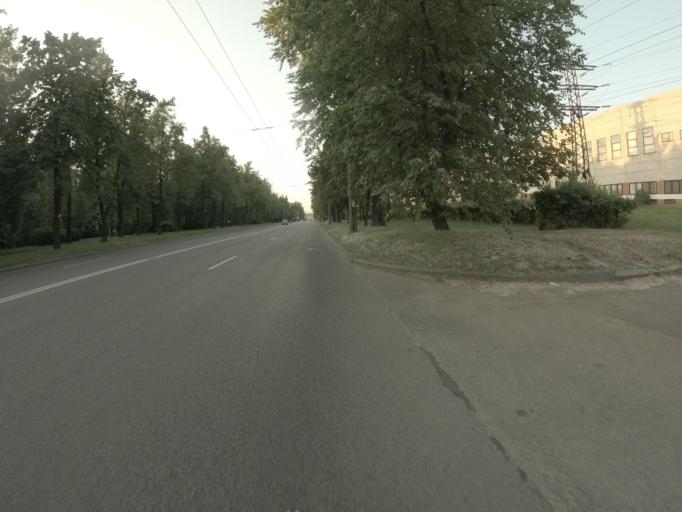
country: RU
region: St.-Petersburg
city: Avtovo
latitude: 59.8744
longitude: 30.2757
